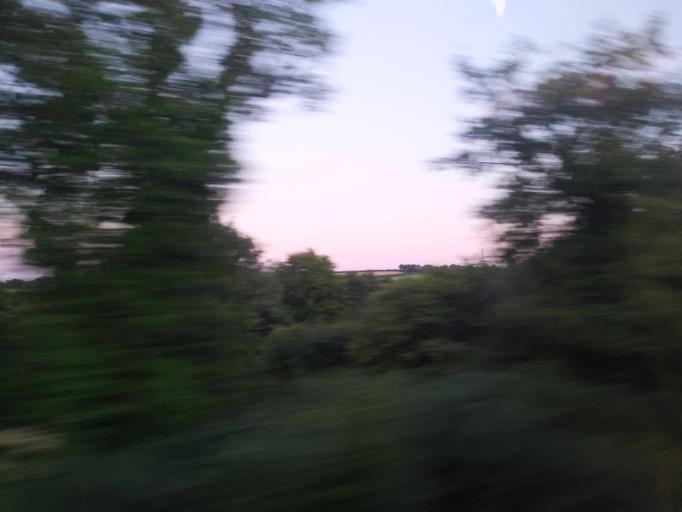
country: GB
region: England
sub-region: Devon
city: South Brent
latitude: 50.4150
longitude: -3.8493
